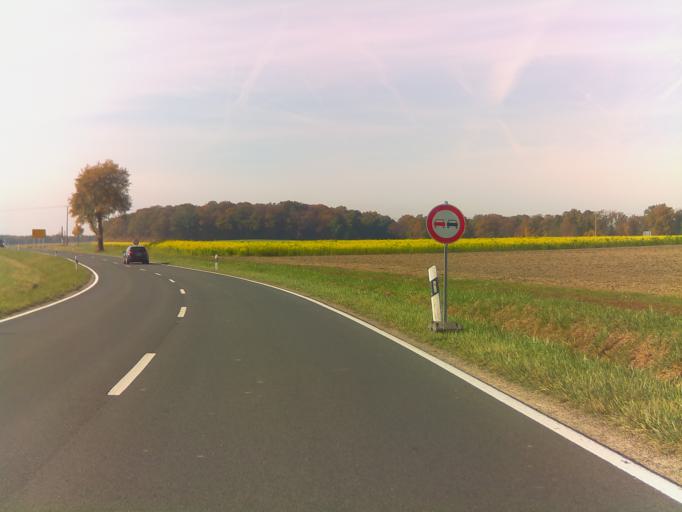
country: DE
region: Bavaria
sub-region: Regierungsbezirk Unterfranken
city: Oberschwarzach
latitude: 49.8494
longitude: 10.3913
